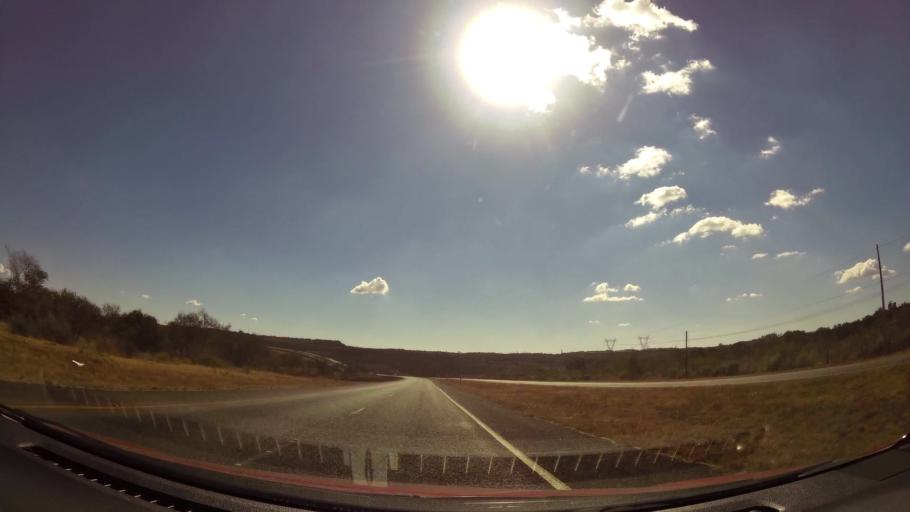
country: ZA
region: North-West
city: Fochville
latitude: -26.4209
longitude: 27.4599
